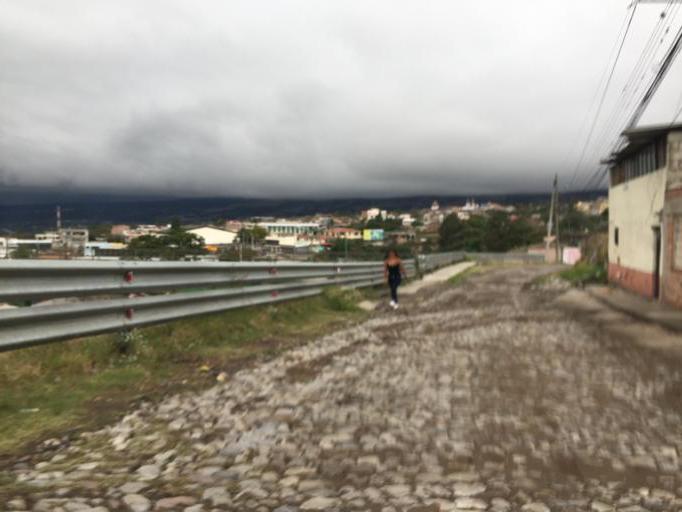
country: EC
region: Imbabura
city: Atuntaqui
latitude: 0.3397
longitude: -78.1722
